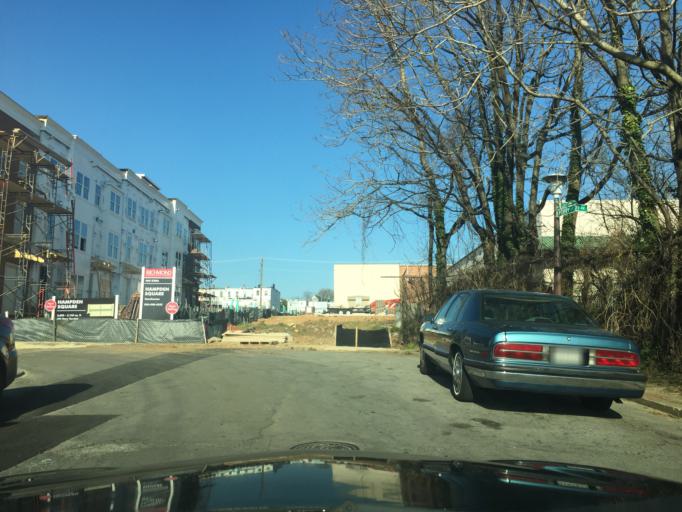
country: US
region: Maryland
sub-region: City of Baltimore
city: Baltimore
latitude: 39.3315
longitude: -76.6373
